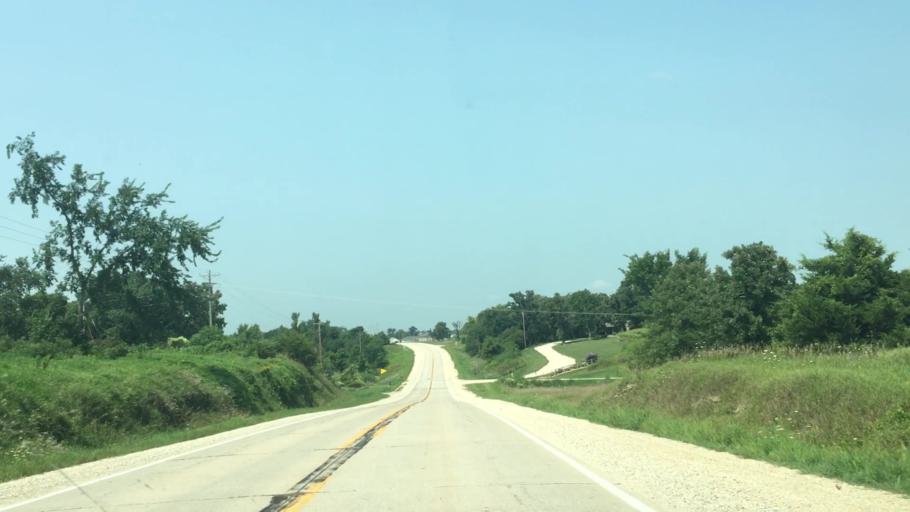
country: US
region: Iowa
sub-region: Fayette County
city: West Union
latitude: 43.1126
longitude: -91.8692
